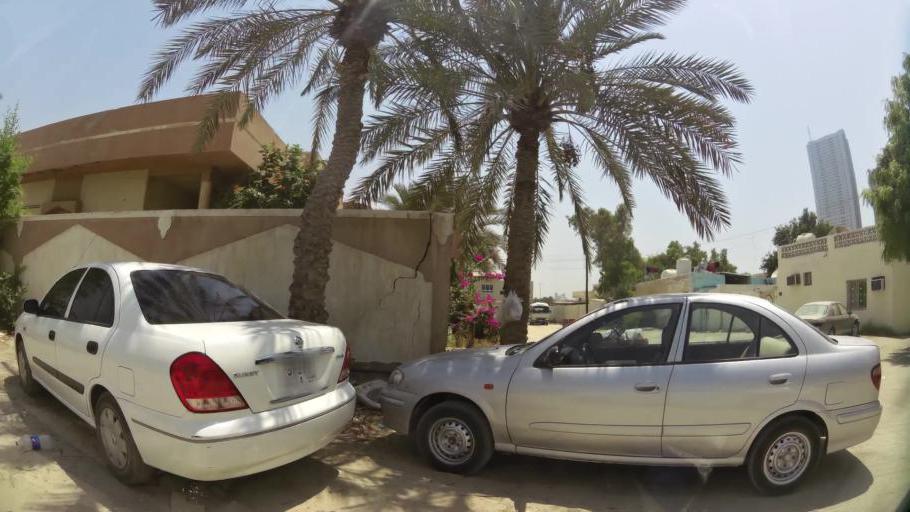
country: AE
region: Ajman
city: Ajman
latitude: 25.4030
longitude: 55.4355
